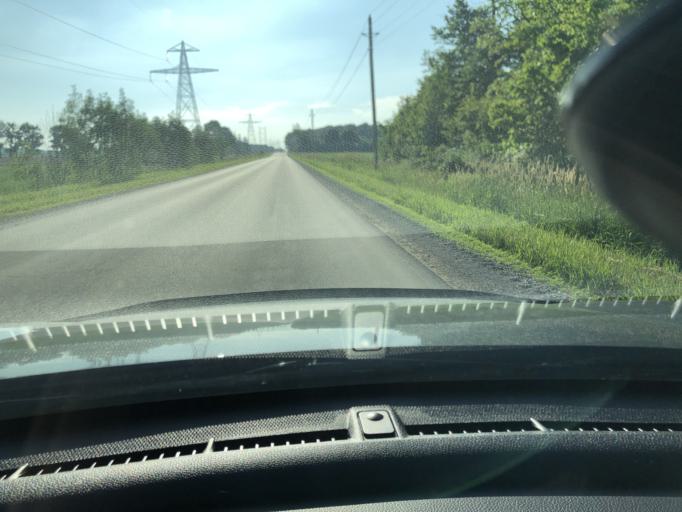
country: CA
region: Ontario
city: Stratford
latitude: 43.3881
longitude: -80.8520
